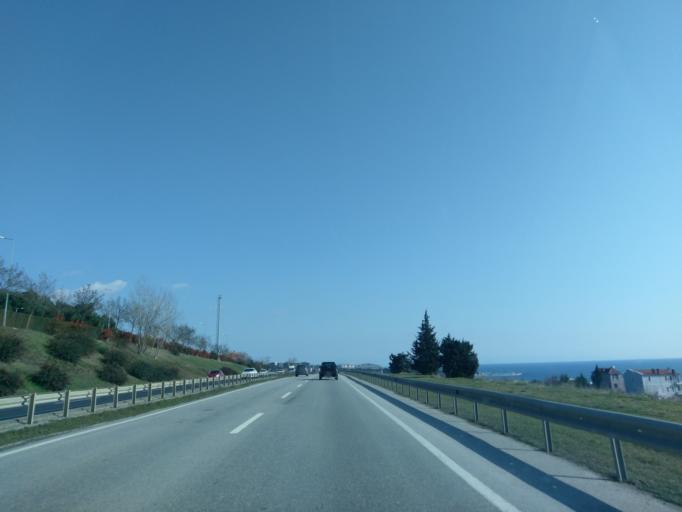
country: TR
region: Istanbul
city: Kumburgaz
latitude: 41.0147
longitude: 28.4909
